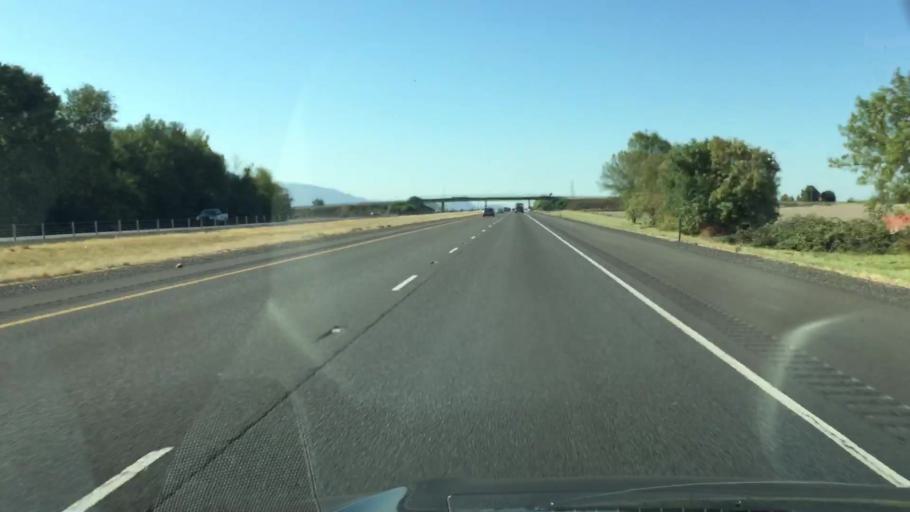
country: US
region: Oregon
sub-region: Linn County
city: Brownsville
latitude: 44.3636
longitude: -123.0618
